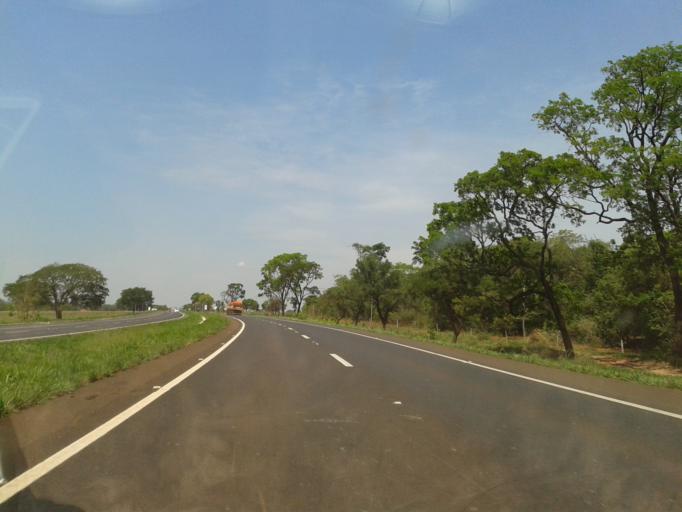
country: BR
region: Minas Gerais
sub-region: Monte Alegre De Minas
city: Monte Alegre de Minas
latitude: -18.8947
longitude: -48.6549
